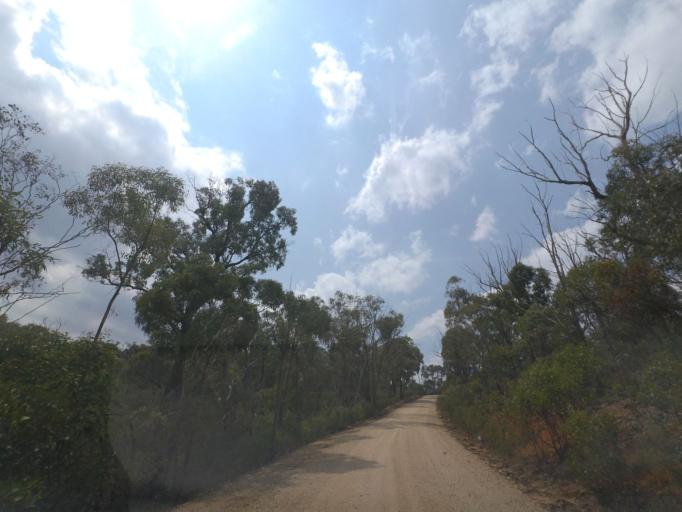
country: AU
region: Victoria
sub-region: Moorabool
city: Bacchus Marsh
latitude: -37.5914
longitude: 144.4363
